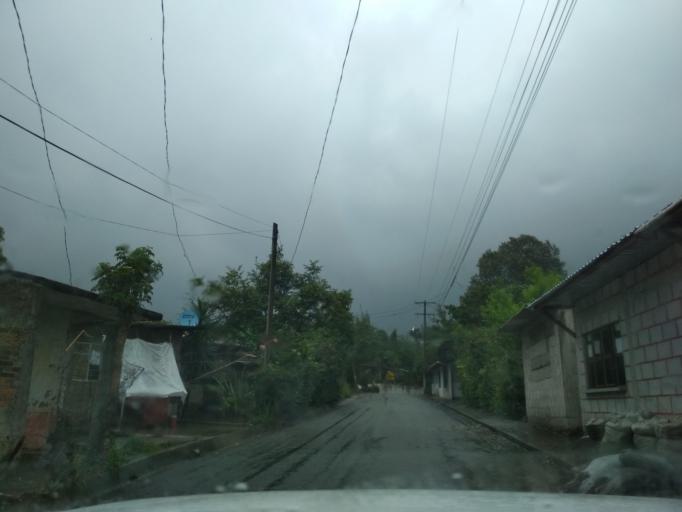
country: MX
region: Veracruz
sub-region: Mariano Escobedo
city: Chicola
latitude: 18.9023
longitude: -97.1172
